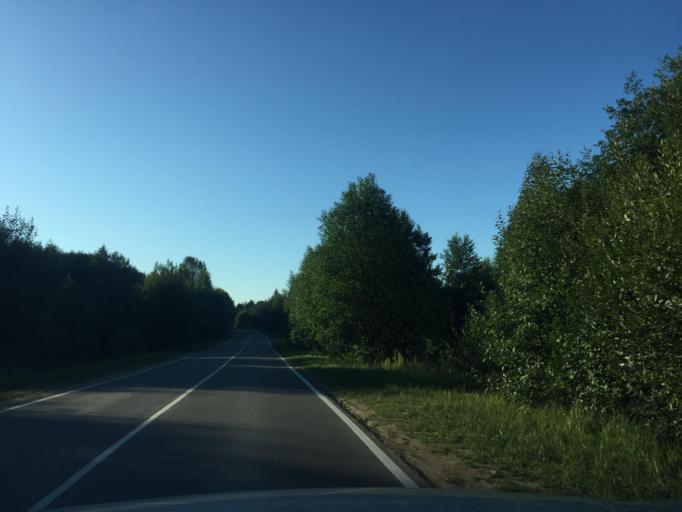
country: RU
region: Leningrad
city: Siverskiy
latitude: 59.3397
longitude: 30.0246
